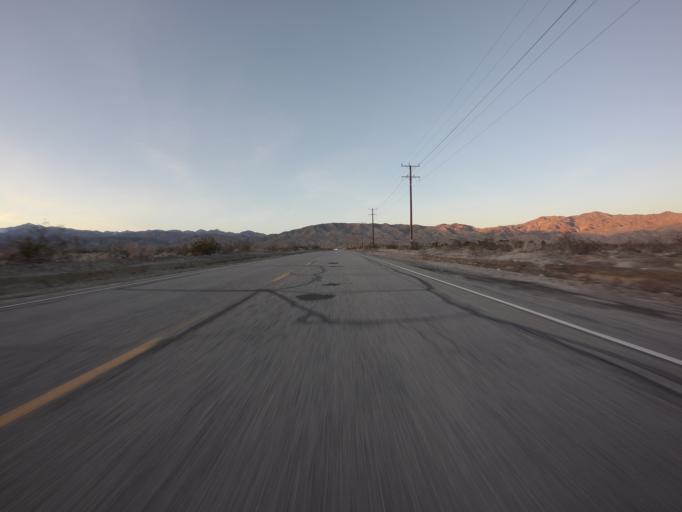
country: US
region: California
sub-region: San Bernardino County
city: Morongo Valley
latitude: 33.9979
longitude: -116.5646
